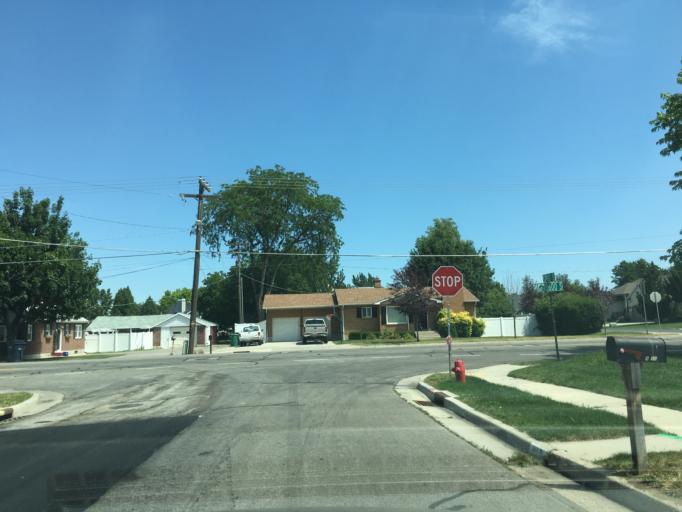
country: US
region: Utah
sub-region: Salt Lake County
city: Sandy City
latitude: 40.5948
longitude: -111.8656
